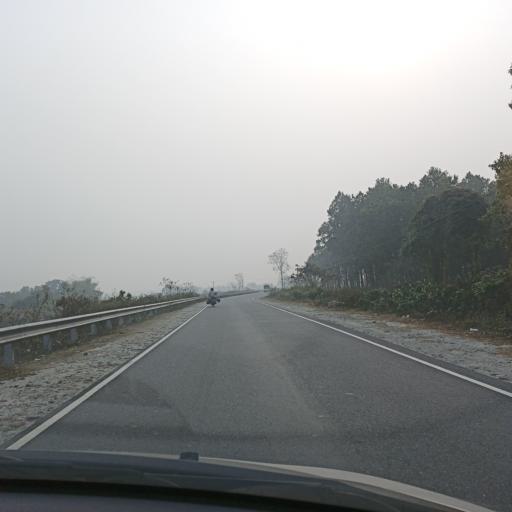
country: IN
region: West Bengal
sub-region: Darjiling
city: Shiliguri
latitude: 26.6726
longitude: 88.5051
